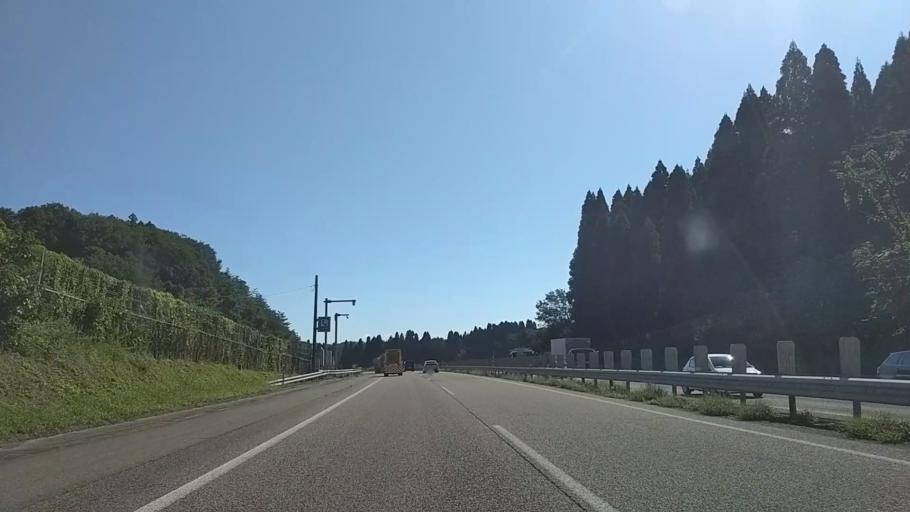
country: JP
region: Toyama
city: Takaoka
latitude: 36.6817
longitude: 137.0479
